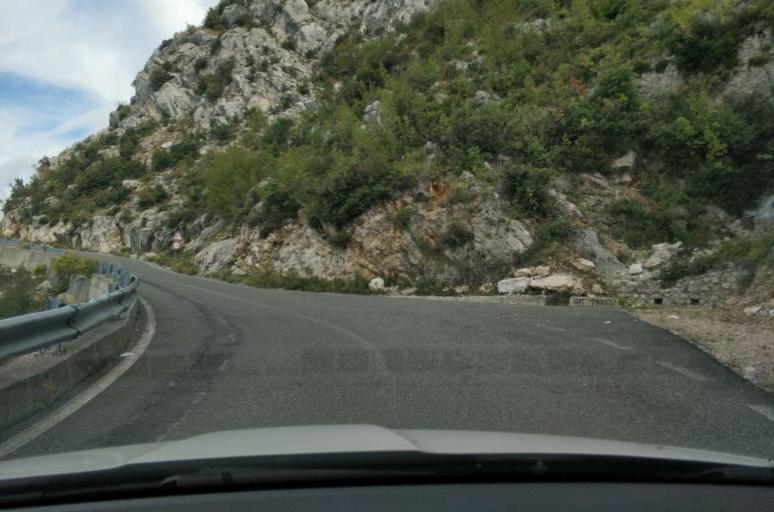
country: AL
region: Durres
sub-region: Rrethi i Krujes
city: Kruje
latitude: 41.5261
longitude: 19.7944
